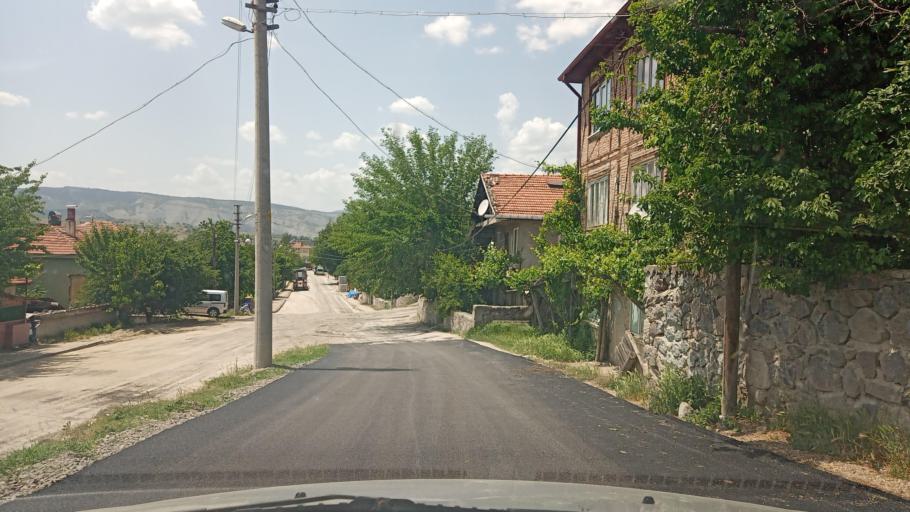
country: TR
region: Bolu
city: Seben
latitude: 40.4081
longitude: 31.5759
